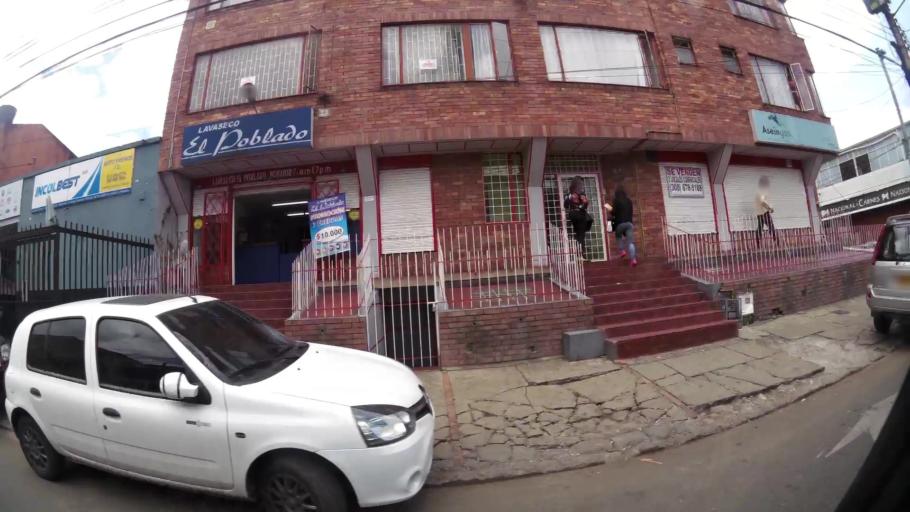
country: CO
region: Bogota D.C.
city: Barrio San Luis
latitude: 4.7169
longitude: -74.0568
